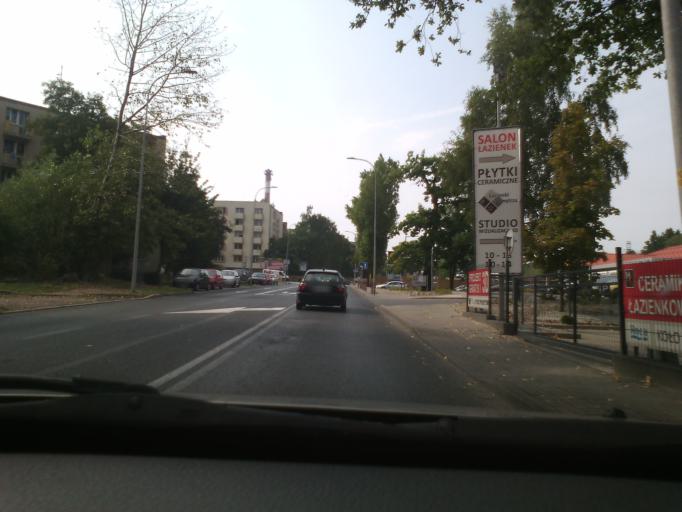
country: PL
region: Lower Silesian Voivodeship
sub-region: Powiat walbrzyski
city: Szczawno-Zdroj
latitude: 50.8110
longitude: 16.2919
